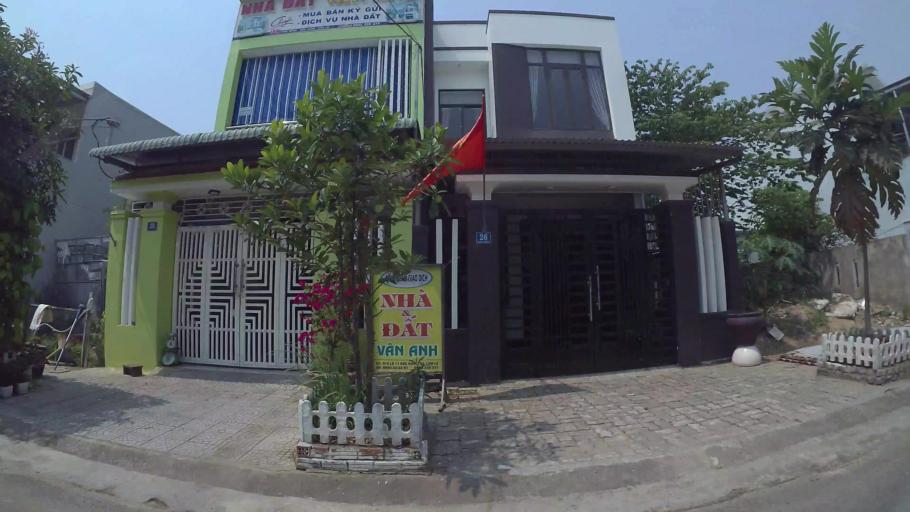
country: VN
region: Da Nang
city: Cam Le
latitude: 15.9915
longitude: 108.2087
